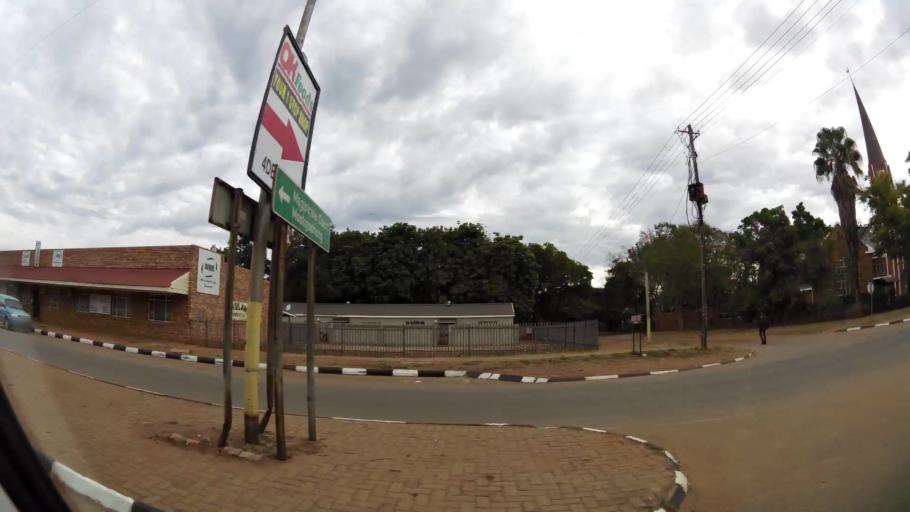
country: ZA
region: Limpopo
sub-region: Waterberg District Municipality
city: Modimolle
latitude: -24.5186
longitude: 28.7113
